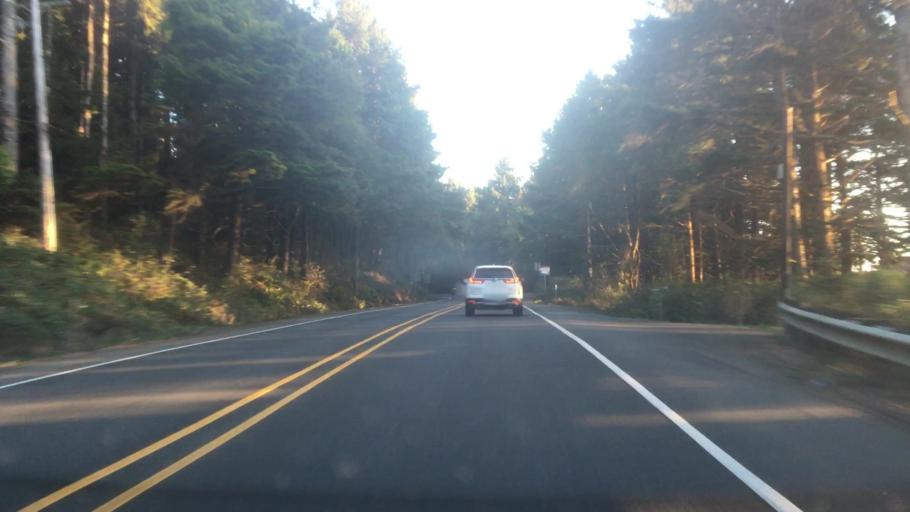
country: US
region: Oregon
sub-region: Clatsop County
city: Cannon Beach
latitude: 45.8437
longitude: -123.9592
